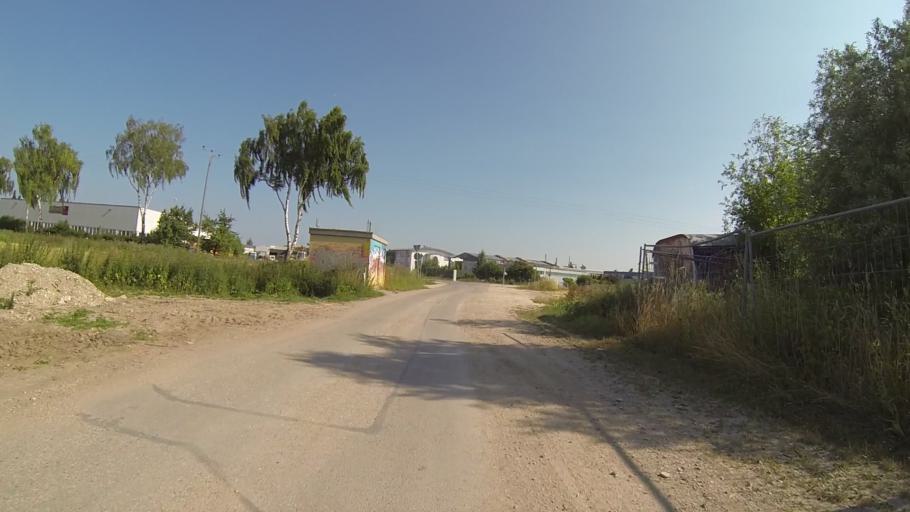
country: DE
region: Baden-Wuerttemberg
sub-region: Tuebingen Region
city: Erbach
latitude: 48.3308
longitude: 9.9027
